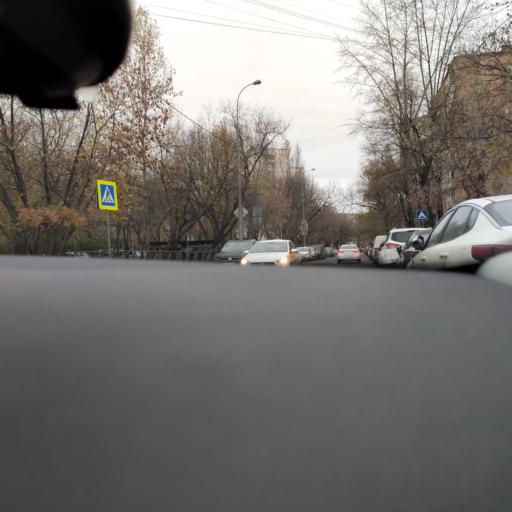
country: RU
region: Moscow
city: Tekstil'shchiki
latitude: 55.7016
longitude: 37.7422
